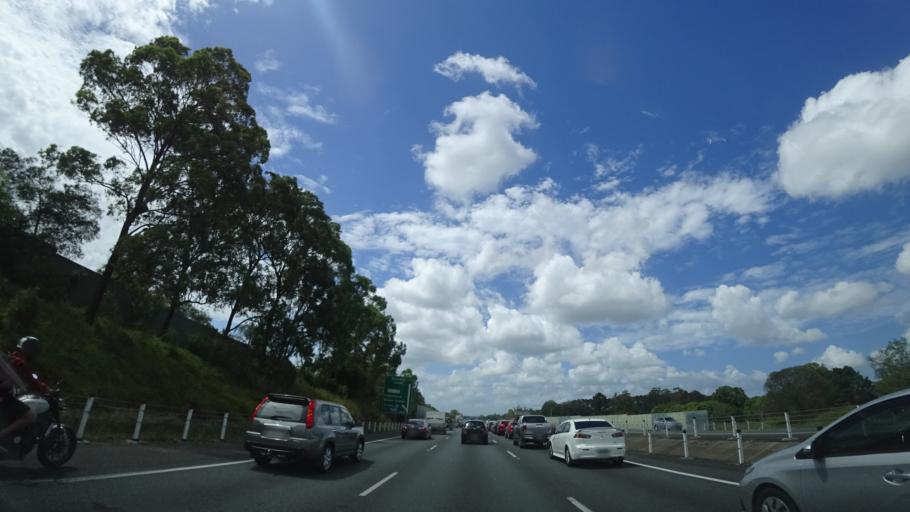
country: AU
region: Queensland
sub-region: Moreton Bay
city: Caboolture South
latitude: -27.1002
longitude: 152.9760
